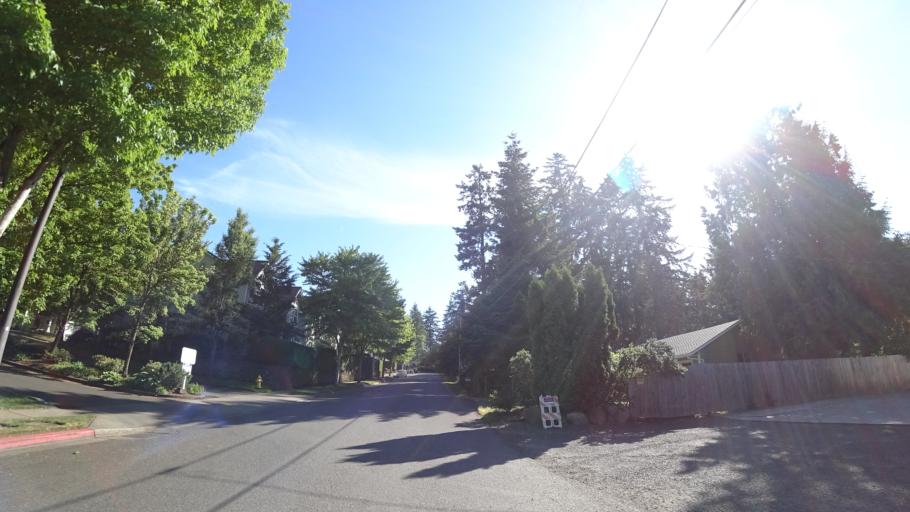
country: US
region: Oregon
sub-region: Washington County
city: Beaverton
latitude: 45.4635
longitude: -122.8041
